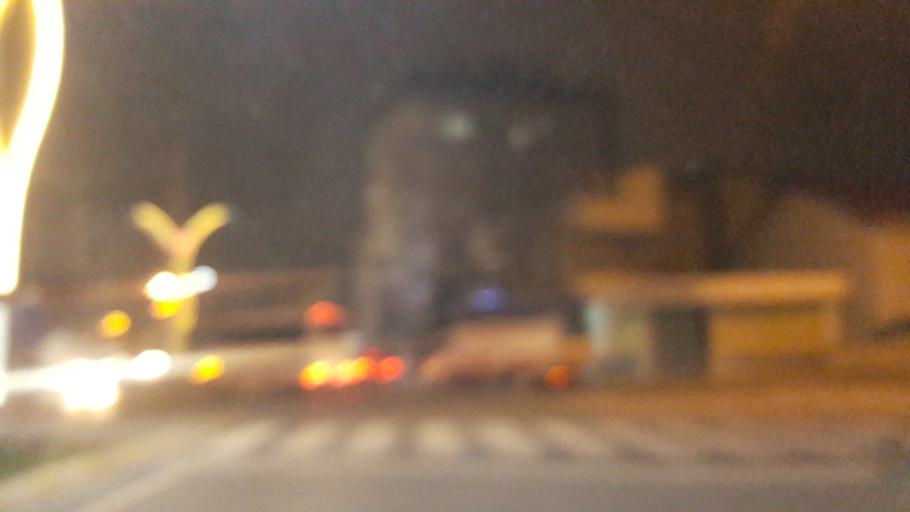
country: TR
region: Kocaeli
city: Darica
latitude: 40.7821
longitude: 29.3971
